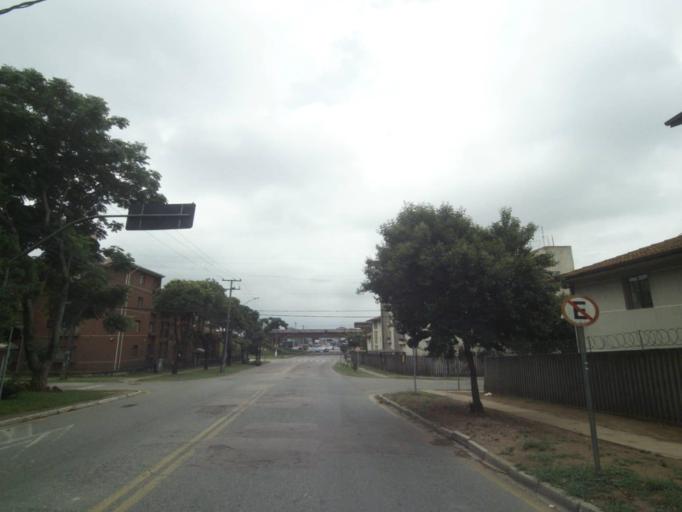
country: BR
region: Parana
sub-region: Curitiba
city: Curitiba
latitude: -25.4838
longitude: -49.3494
